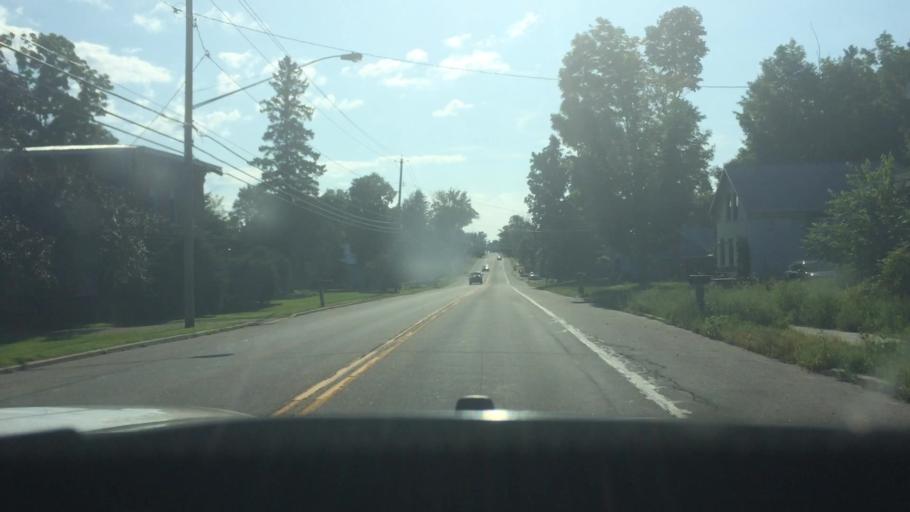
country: US
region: New York
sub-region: Franklin County
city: Malone
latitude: 44.8137
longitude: -74.3903
